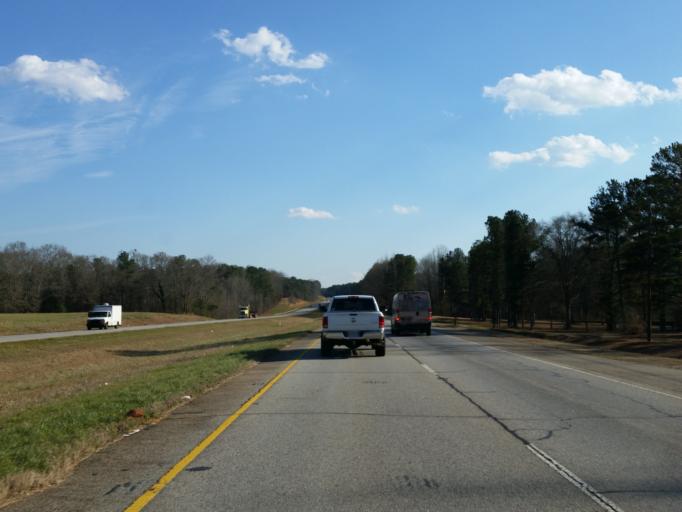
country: US
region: Georgia
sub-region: Spalding County
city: Griffin
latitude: 33.1596
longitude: -84.2557
